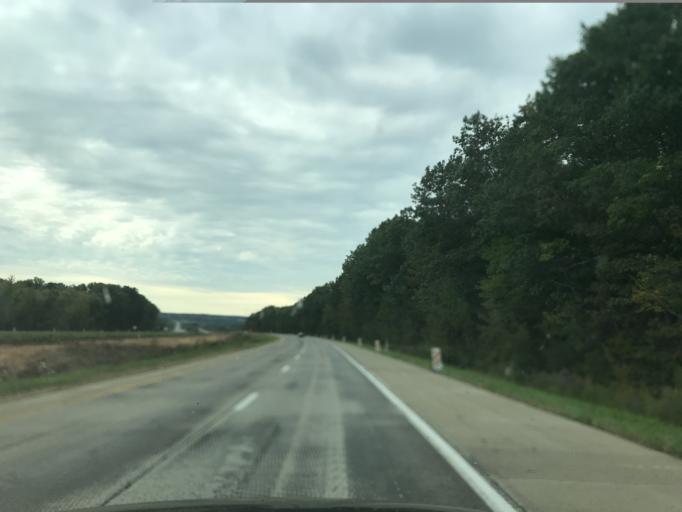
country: US
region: Pennsylvania
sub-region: Erie County
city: Fairview
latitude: 42.0108
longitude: -80.1544
